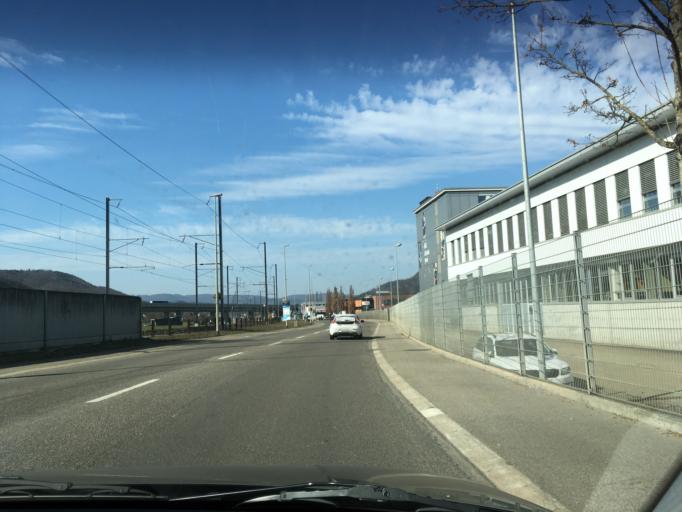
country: CH
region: Basel-Landschaft
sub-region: Bezirk Sissach
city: Sissach
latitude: 47.4649
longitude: 7.8062
